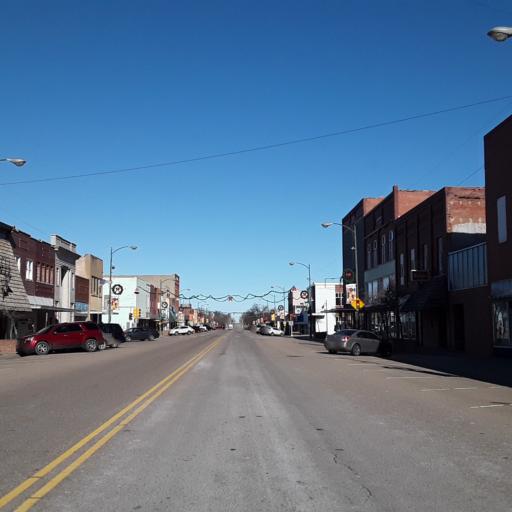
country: US
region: Kansas
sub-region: Pawnee County
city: Larned
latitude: 38.1775
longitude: -99.0983
